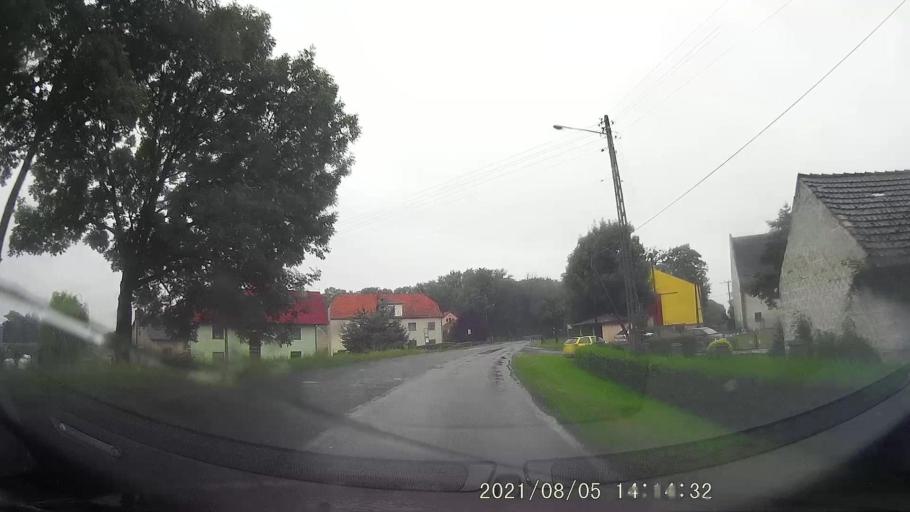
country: PL
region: Opole Voivodeship
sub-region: Powiat prudnicki
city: Biala
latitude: 50.4676
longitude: 17.7400
